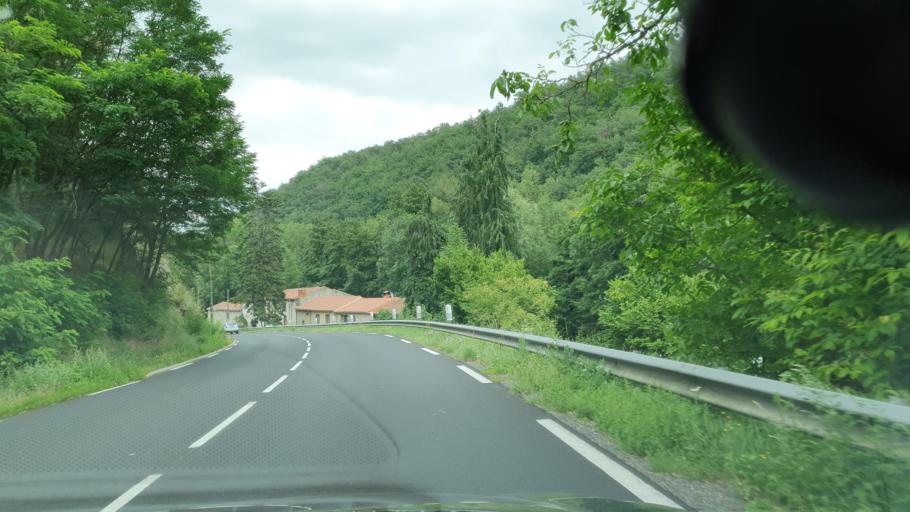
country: FR
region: Auvergne
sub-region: Departement du Puy-de-Dome
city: Champeix
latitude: 45.5795
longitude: 3.0816
